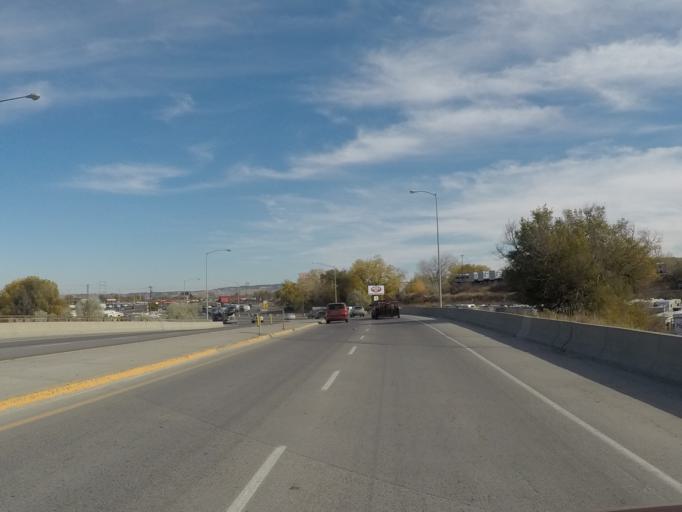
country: US
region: Montana
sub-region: Yellowstone County
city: Billings
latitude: 45.7960
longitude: -108.4654
